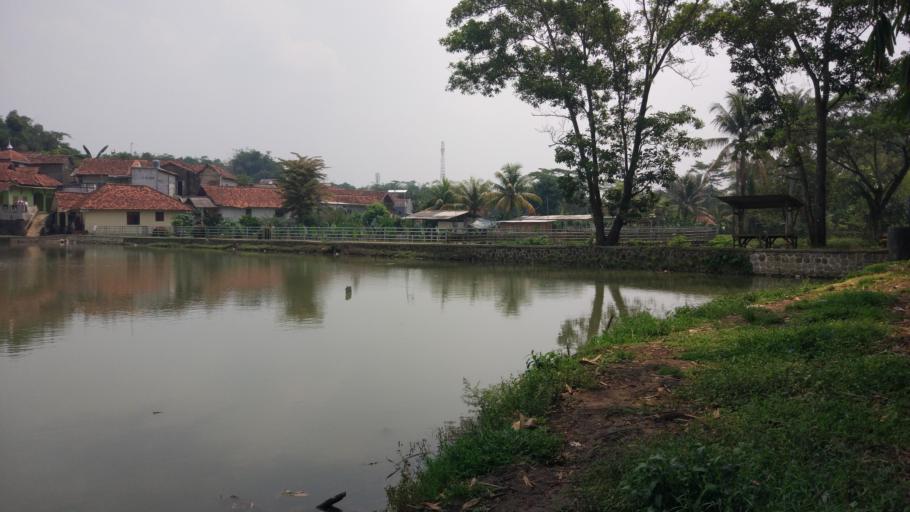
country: ID
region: West Java
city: Ciampea
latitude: -6.5742
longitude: 106.7303
